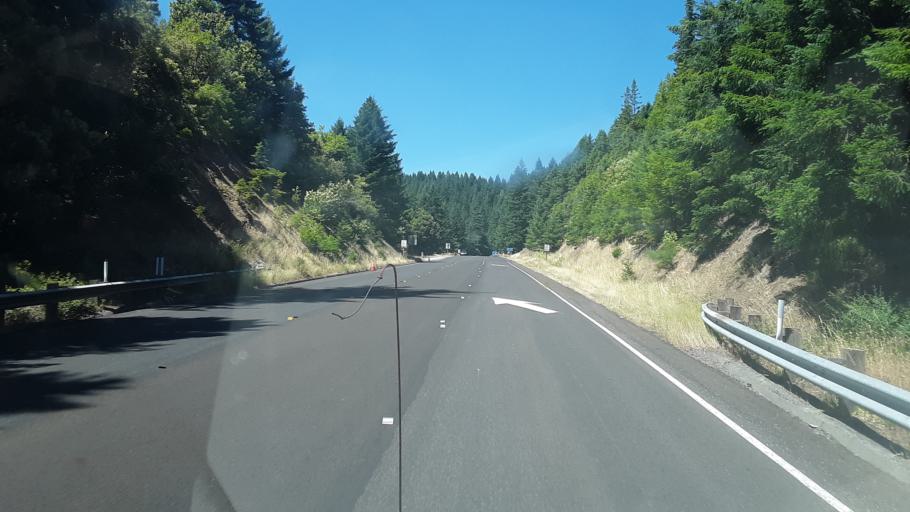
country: US
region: Oregon
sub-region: Josephine County
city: Cave Junction
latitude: 41.9624
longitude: -123.7463
